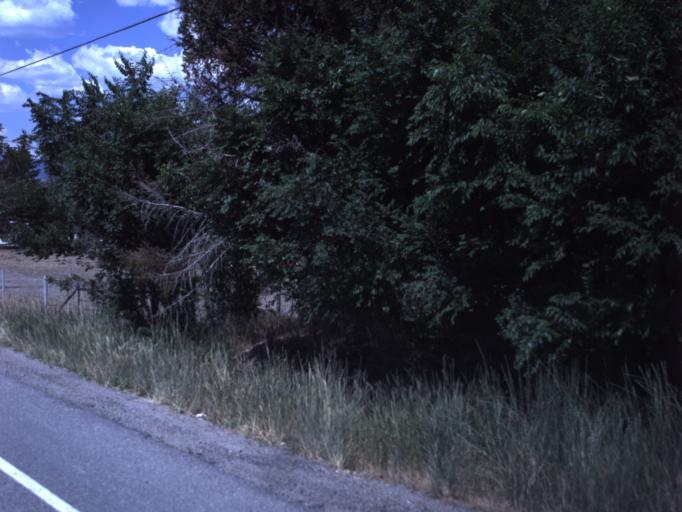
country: US
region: Utah
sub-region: Carbon County
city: Price
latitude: 39.5651
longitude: -110.8159
